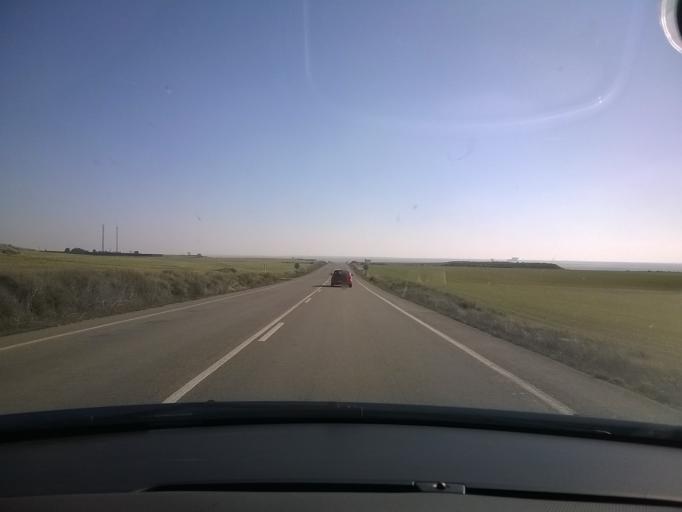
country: ES
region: Aragon
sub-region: Provincia de Zaragoza
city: Bujaraloz
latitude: 41.5111
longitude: -0.1677
